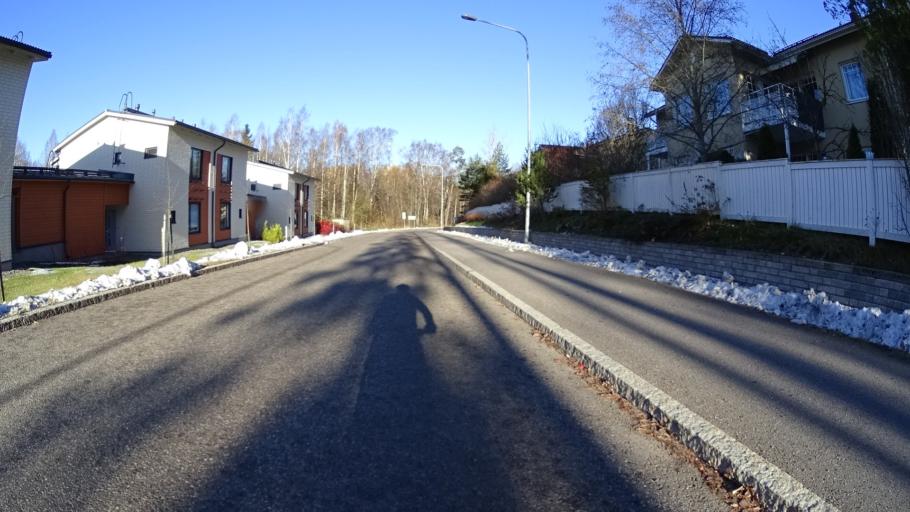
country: FI
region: Uusimaa
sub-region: Helsinki
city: Kauniainen
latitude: 60.2075
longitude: 24.7181
